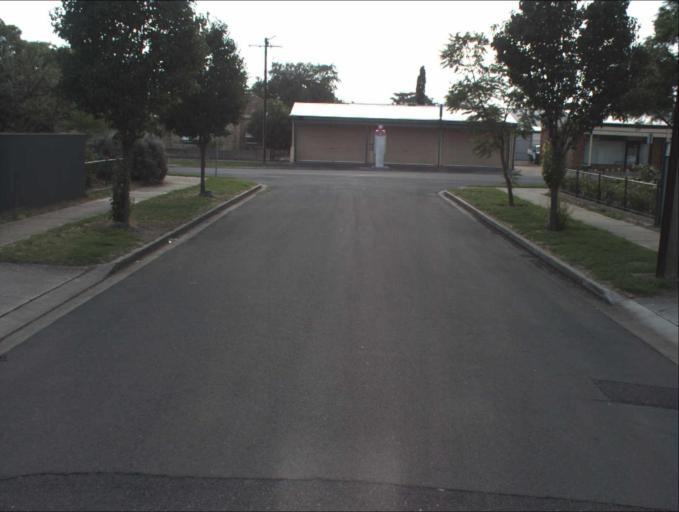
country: AU
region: South Australia
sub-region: Port Adelaide Enfield
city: Klemzig
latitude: -34.8776
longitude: 138.6242
